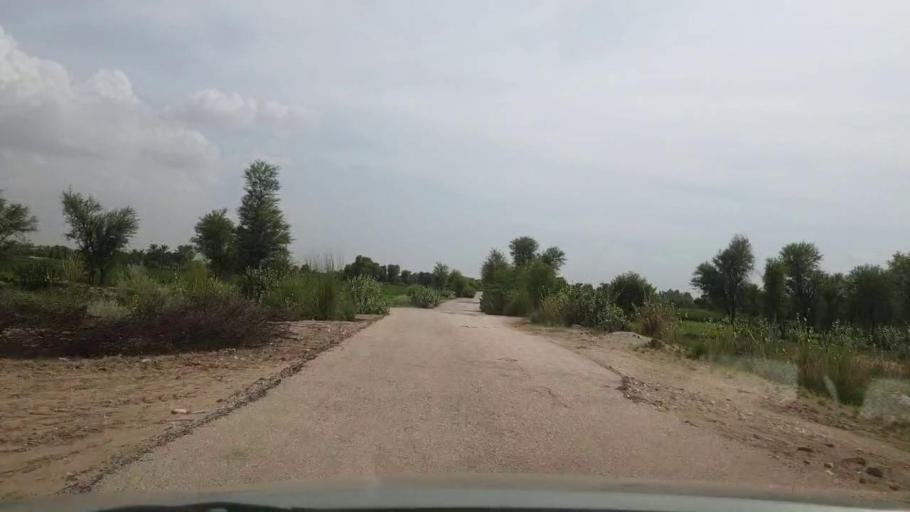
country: PK
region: Sindh
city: Kot Diji
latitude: 27.1188
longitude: 69.0252
